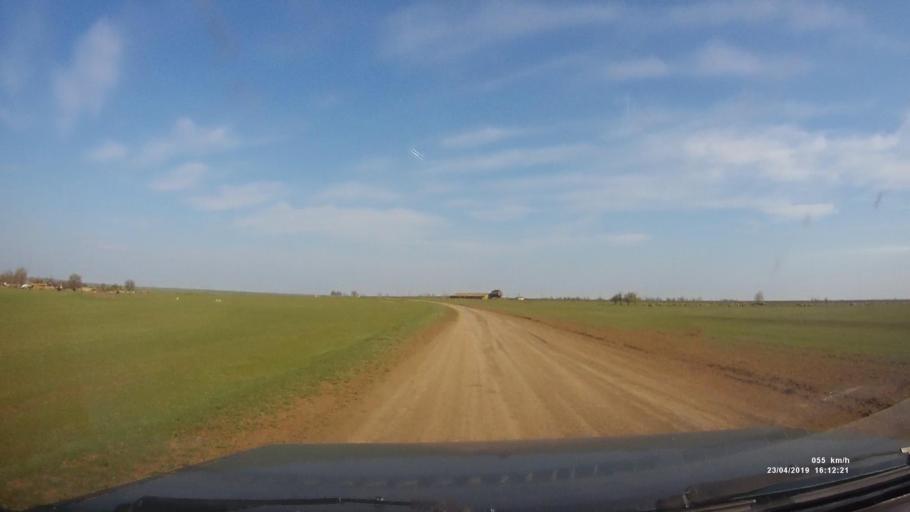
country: RU
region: Kalmykiya
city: Priyutnoye
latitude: 46.4668
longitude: 43.1255
